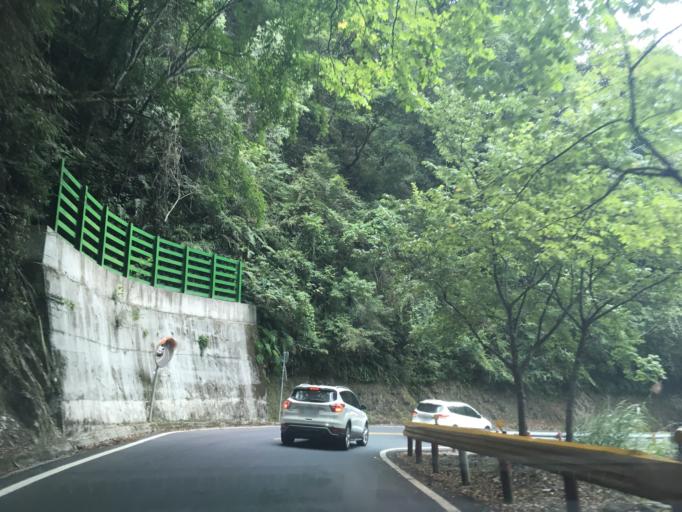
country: TW
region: Taiwan
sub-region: Hualien
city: Hualian
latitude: 24.2064
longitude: 121.4333
